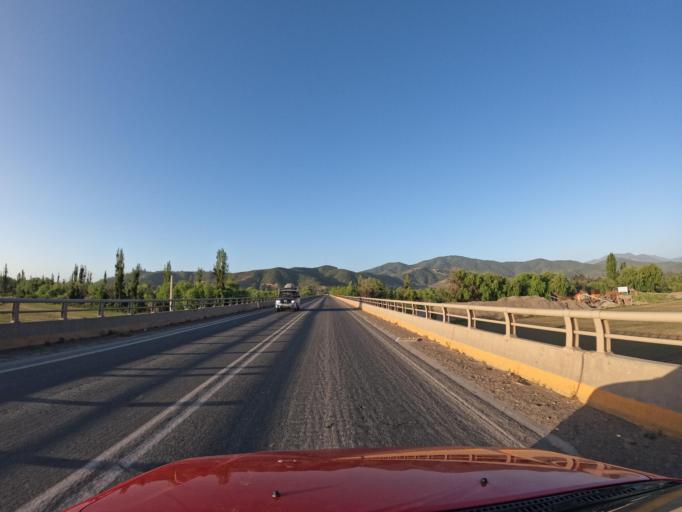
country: CL
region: O'Higgins
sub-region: Provincia de Cachapoal
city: San Vicente
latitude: -34.2799
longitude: -71.3652
